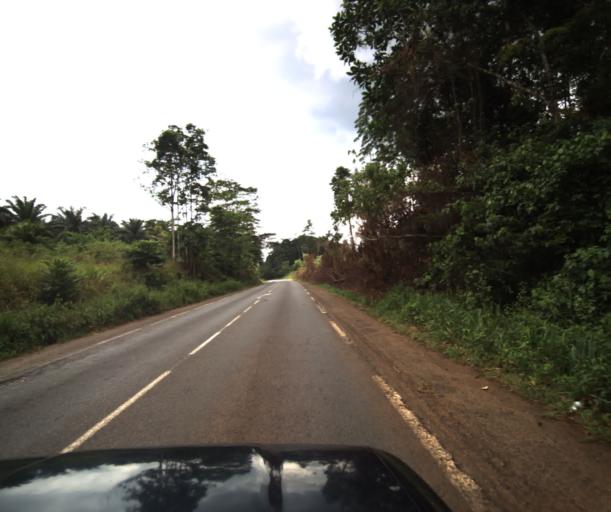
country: CM
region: Centre
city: Eseka
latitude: 3.8910
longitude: 10.7621
